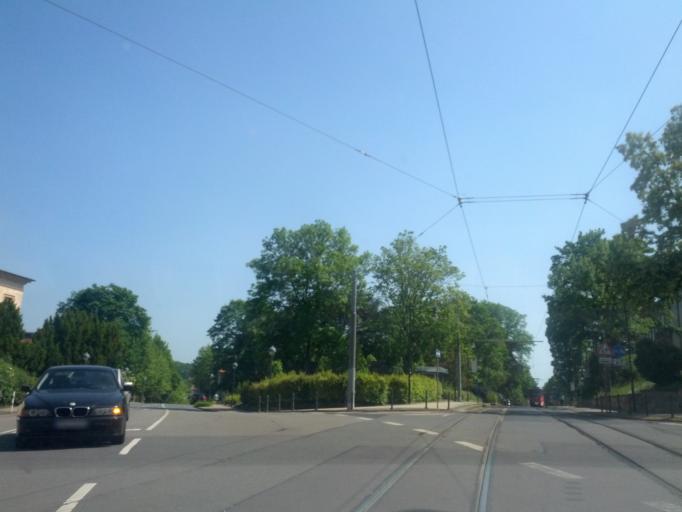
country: DE
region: Thuringia
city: Gotha
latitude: 50.9447
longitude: 10.7109
